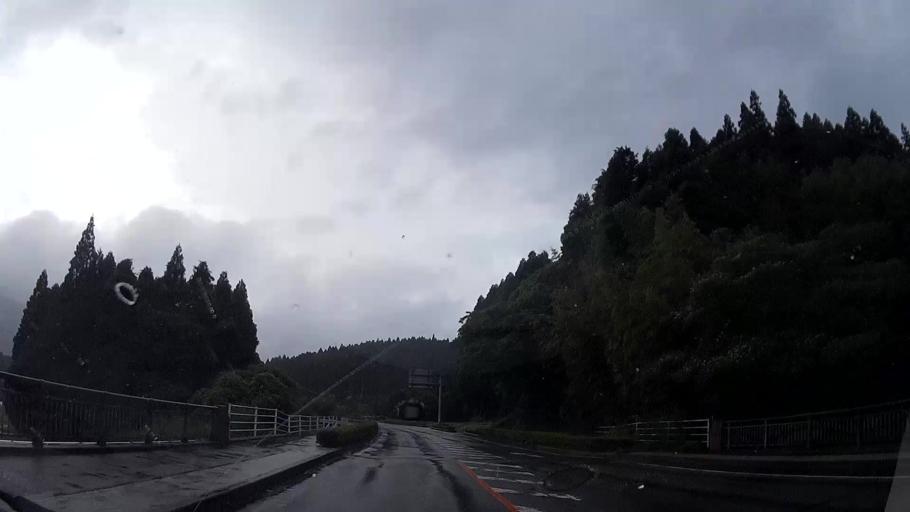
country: JP
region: Kumamoto
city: Aso
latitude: 32.8550
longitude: 131.0180
